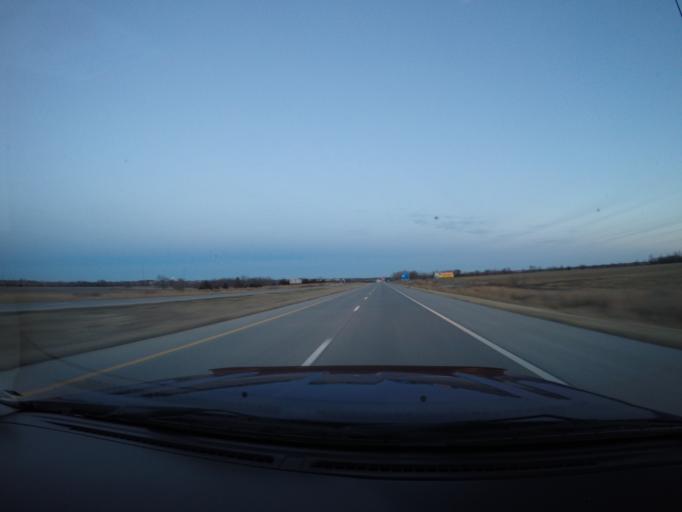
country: US
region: Kansas
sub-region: Geary County
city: Junction City
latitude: 39.0005
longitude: -96.8955
